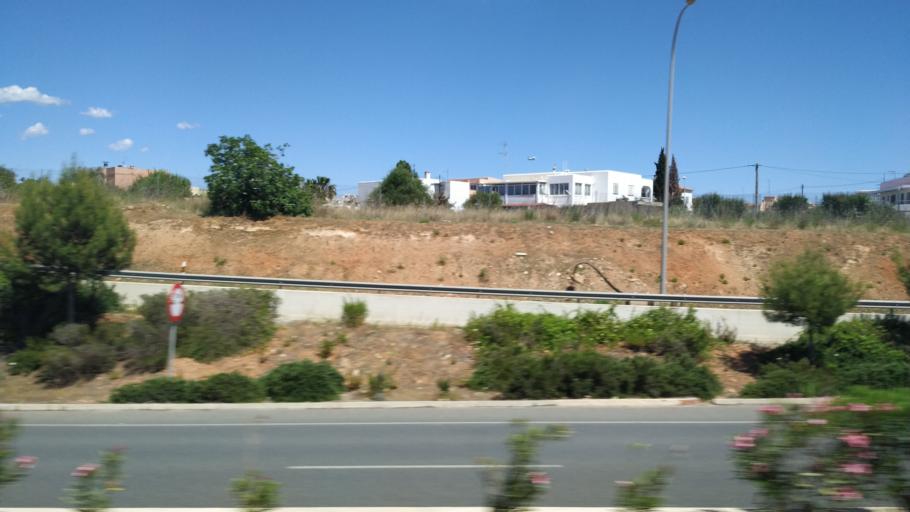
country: ES
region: Balearic Islands
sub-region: Illes Balears
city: Ibiza
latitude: 38.8939
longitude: 1.4006
